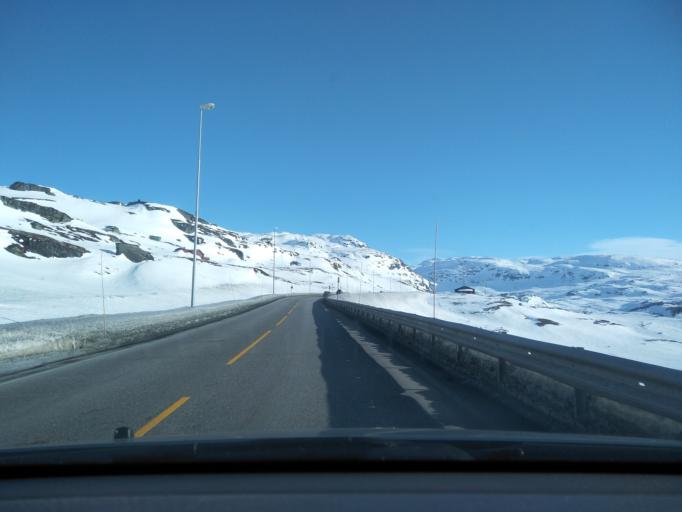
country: NO
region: Aust-Agder
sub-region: Bykle
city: Hovden
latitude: 59.8423
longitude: 6.9768
